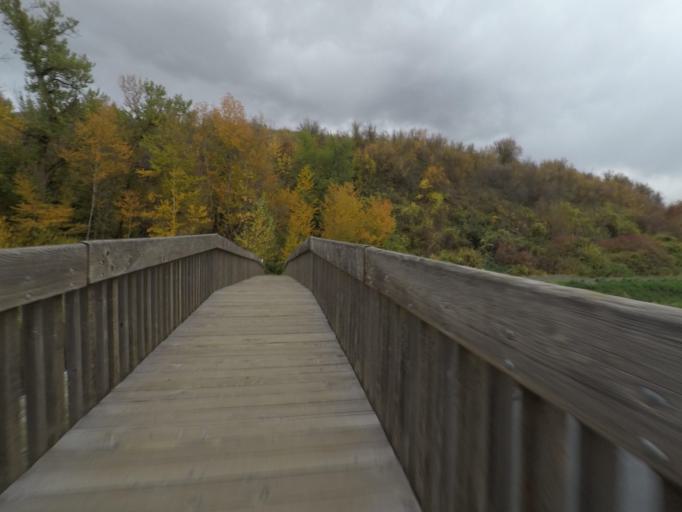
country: US
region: Washington
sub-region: Walla Walla County
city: Walla Walla East
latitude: 46.0801
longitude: -118.2570
